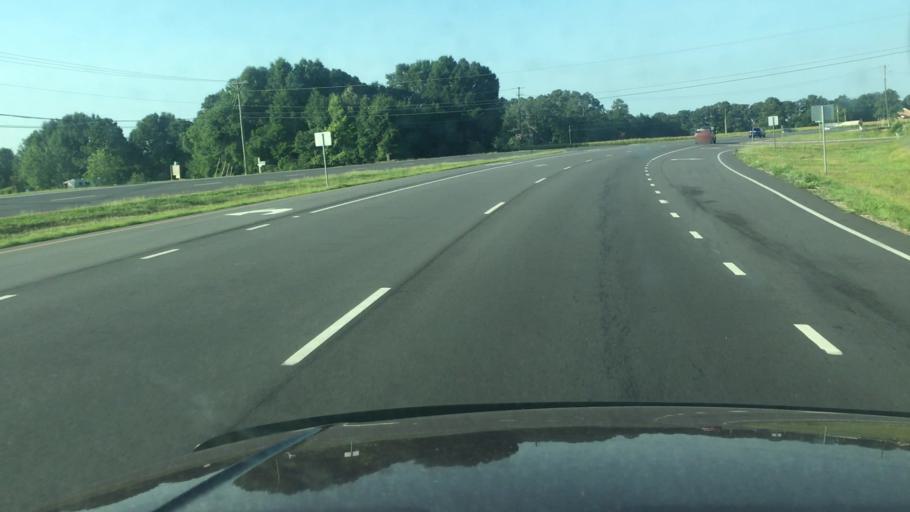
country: US
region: North Carolina
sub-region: Cumberland County
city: Hope Mills
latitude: 34.9371
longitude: -78.8476
